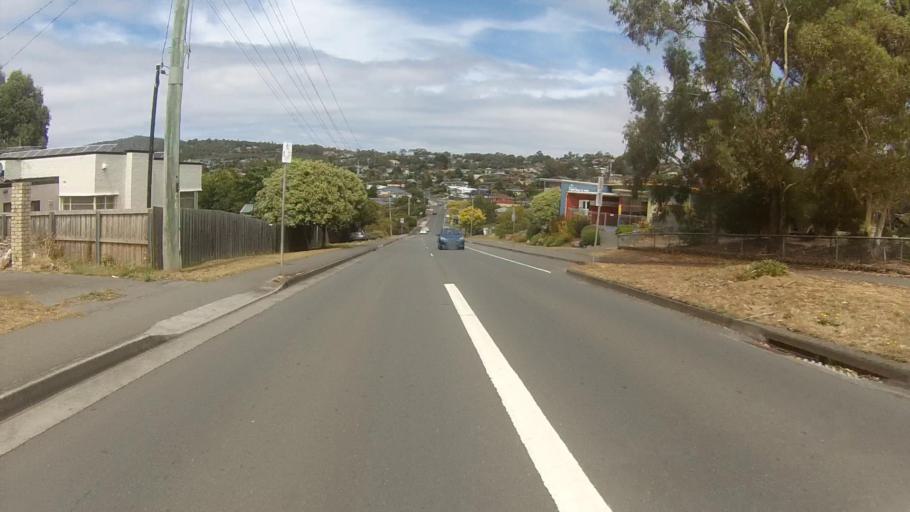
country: AU
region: Tasmania
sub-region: Kingborough
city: Blackmans Bay
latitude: -42.9970
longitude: 147.3228
